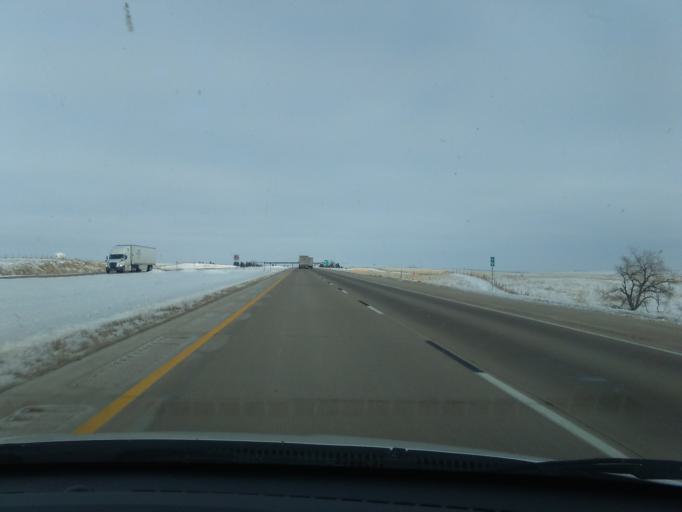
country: US
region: Nebraska
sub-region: Cheyenne County
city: Sidney
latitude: 41.1129
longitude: -102.7760
